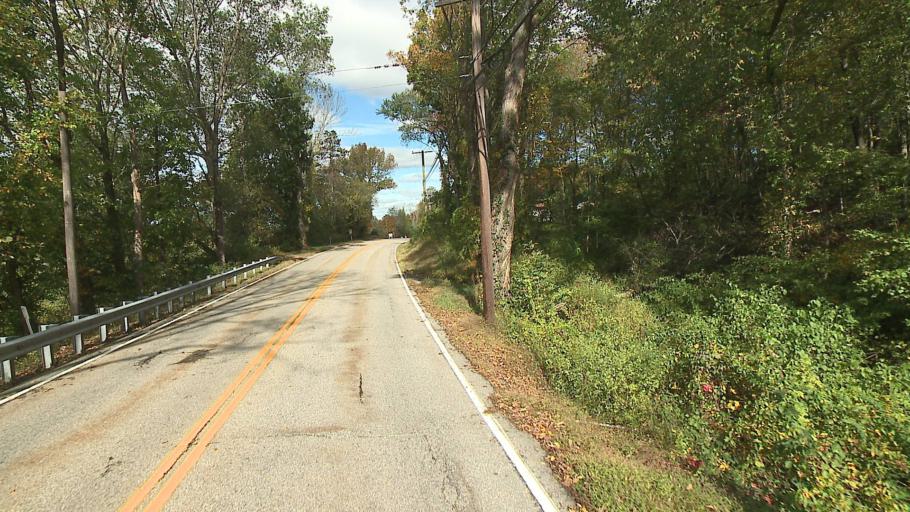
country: US
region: Connecticut
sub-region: Windham County
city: Putnam
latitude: 41.8892
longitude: -71.8771
